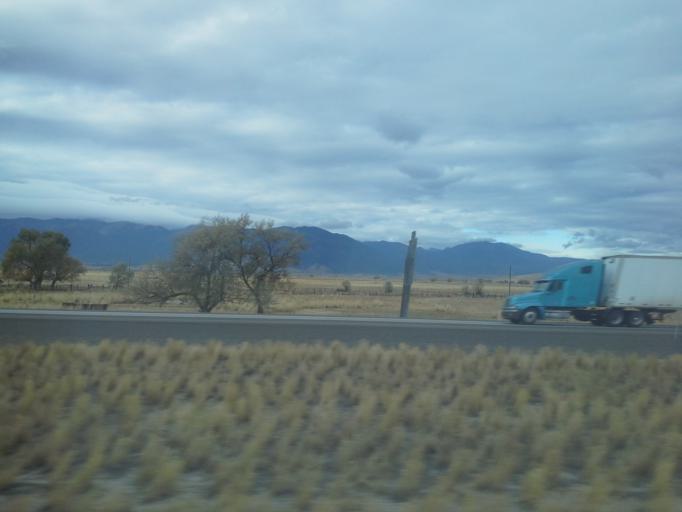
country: US
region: Oregon
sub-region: Baker County
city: Baker City
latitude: 44.8786
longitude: -117.8179
